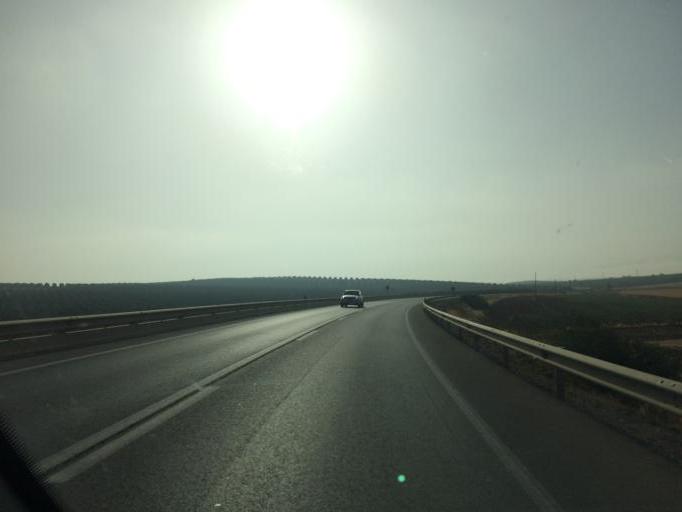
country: ES
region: Andalusia
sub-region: Provincia de Malaga
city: Campillos
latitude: 37.0520
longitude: -4.8092
